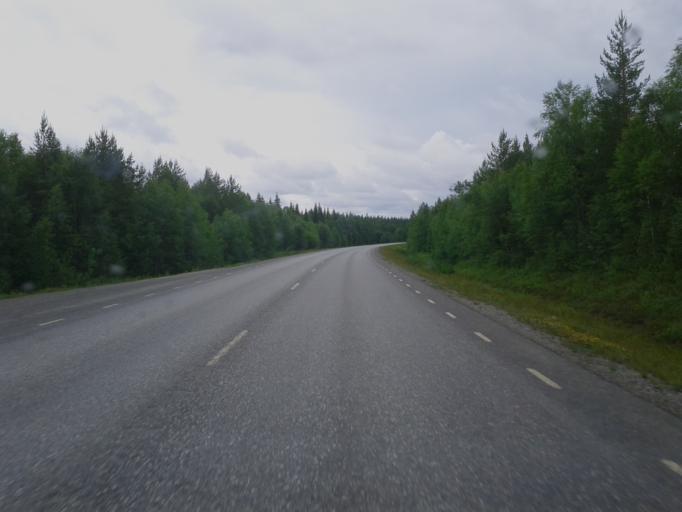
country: SE
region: Vaesterbotten
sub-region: Skelleftea Kommun
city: Langsele
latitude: 64.8843
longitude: 20.2084
